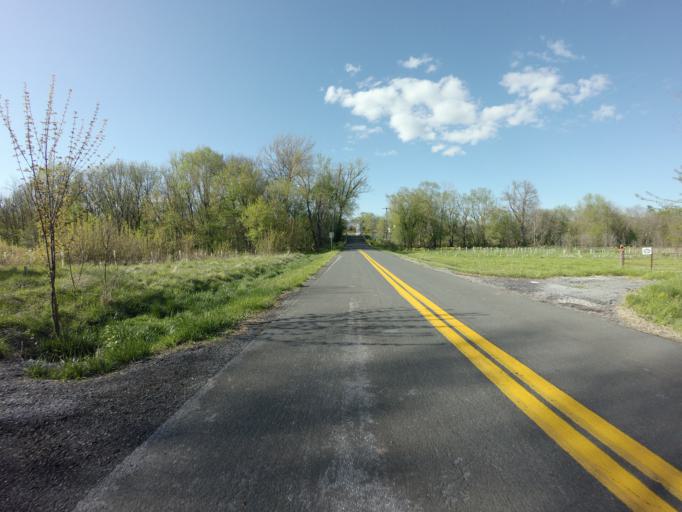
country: US
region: Maryland
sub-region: Frederick County
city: Emmitsburg
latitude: 39.6293
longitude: -77.2885
